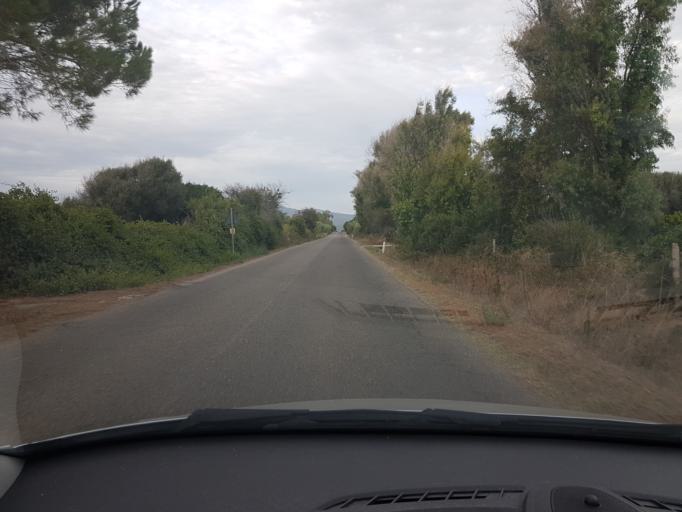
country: IT
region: Sardinia
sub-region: Provincia di Oristano
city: Riola Sardo
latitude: 40.0060
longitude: 8.5390
